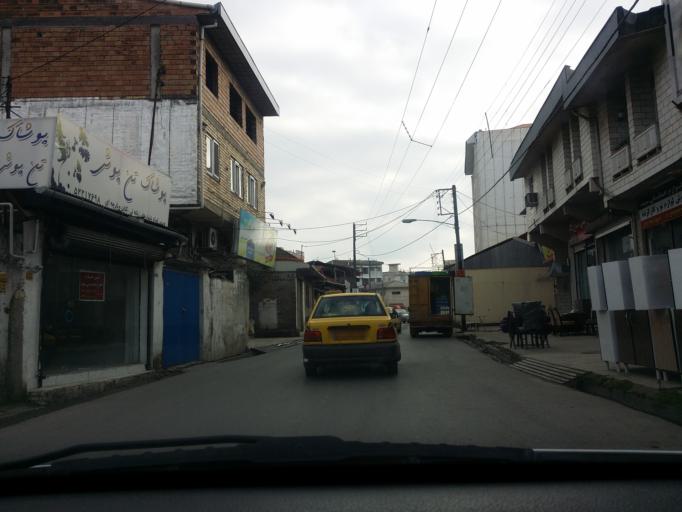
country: IR
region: Mazandaran
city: Chalus
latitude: 36.6571
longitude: 51.4129
